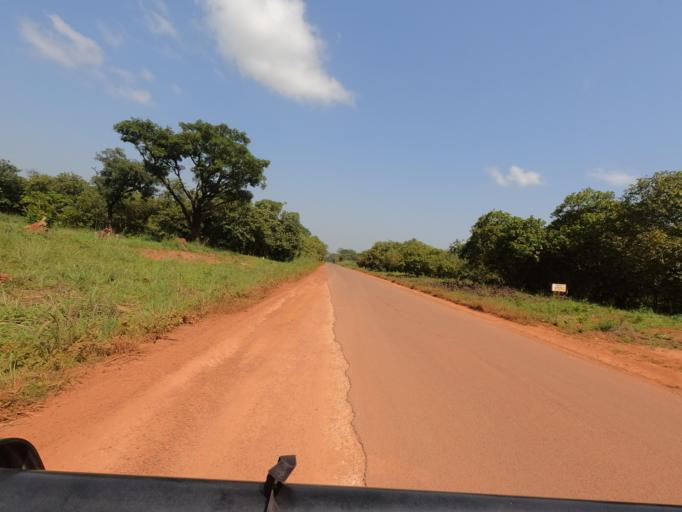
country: GW
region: Oio
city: Bissora
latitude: 12.3212
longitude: -15.7586
